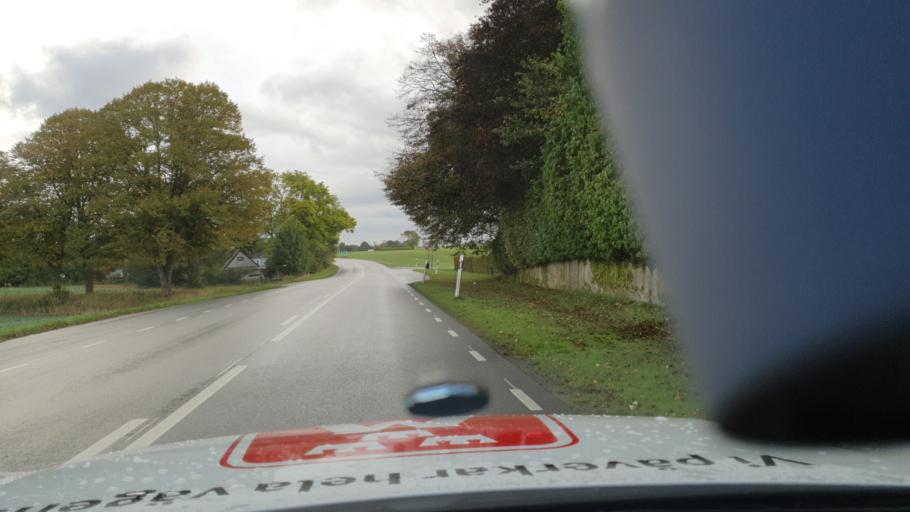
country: SE
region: Skane
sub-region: Svedala Kommun
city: Svedala
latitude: 55.4530
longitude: 13.1922
